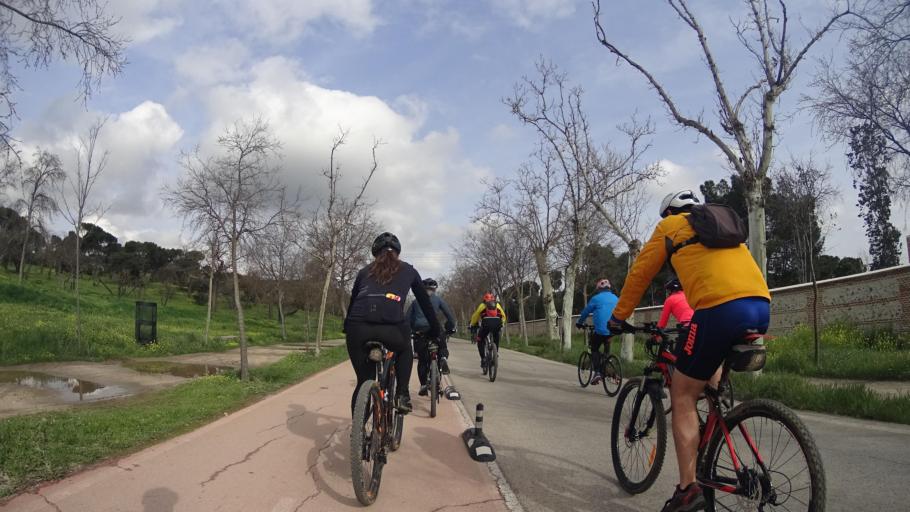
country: ES
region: Madrid
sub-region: Provincia de Madrid
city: Moncloa-Aravaca
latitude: 40.4232
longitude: -3.7318
